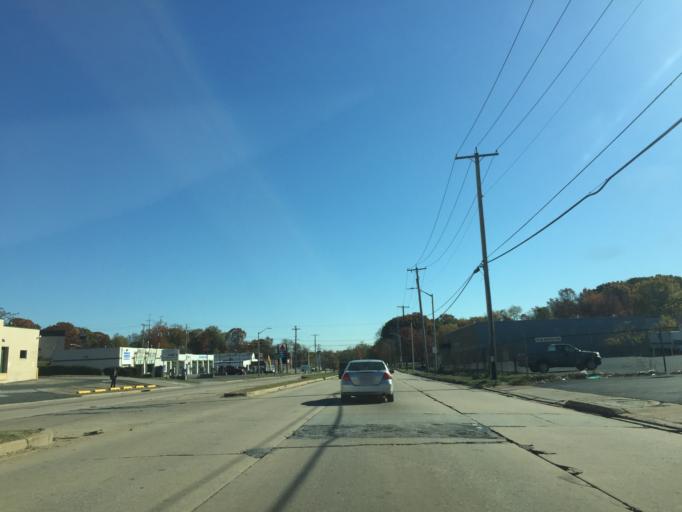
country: US
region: Maryland
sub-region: Baltimore County
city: Baltimore Highlands
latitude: 39.2454
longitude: -76.6344
